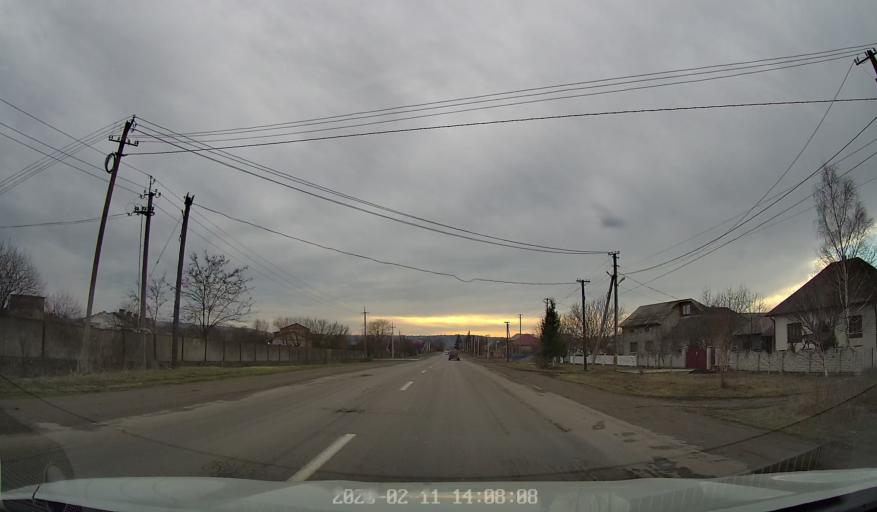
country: RO
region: Botosani
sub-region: Comuna Darabani
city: Bajura
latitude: 48.2403
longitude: 26.5478
